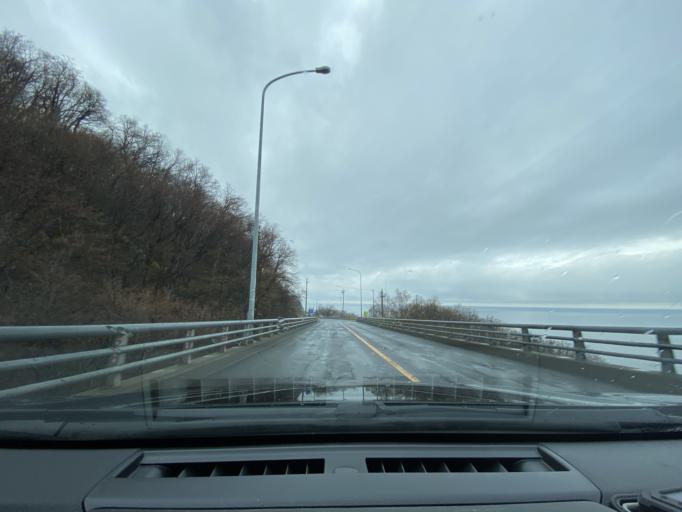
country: JP
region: Hokkaido
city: Rumoi
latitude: 43.8168
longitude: 141.4212
